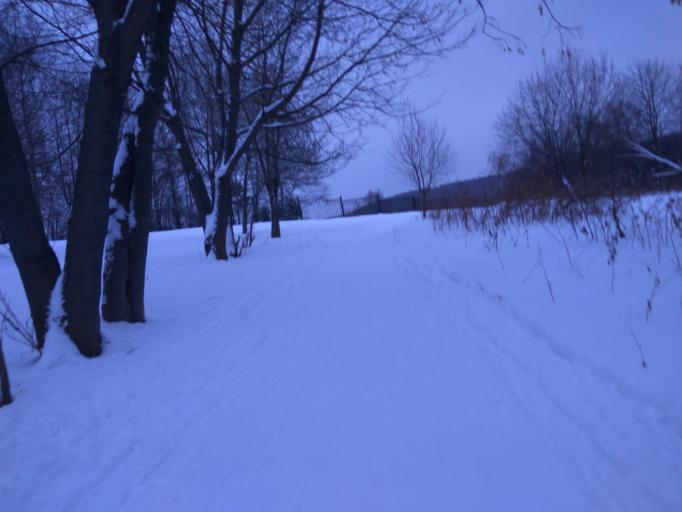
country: RU
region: Moscow
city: Orekhovo-Borisovo Severnoye
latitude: 55.6069
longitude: 37.6926
